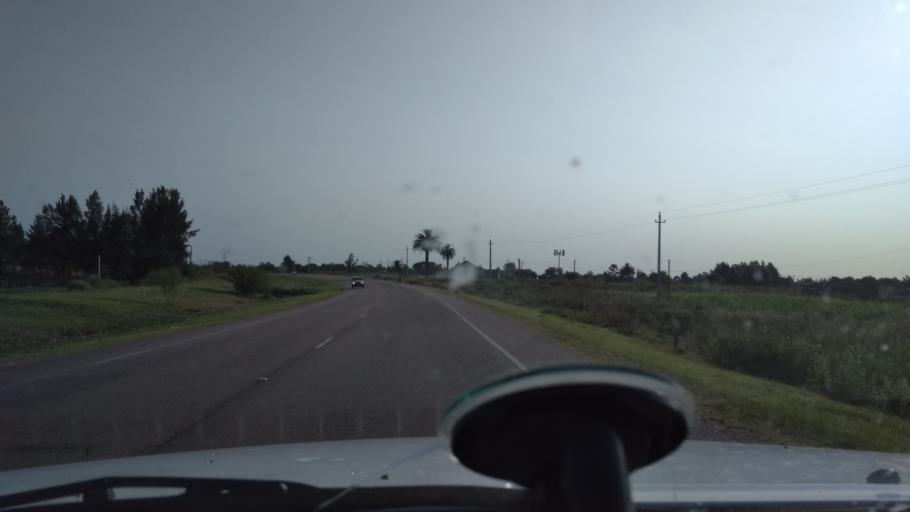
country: UY
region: Canelones
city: Sauce
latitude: -34.6552
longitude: -56.0541
